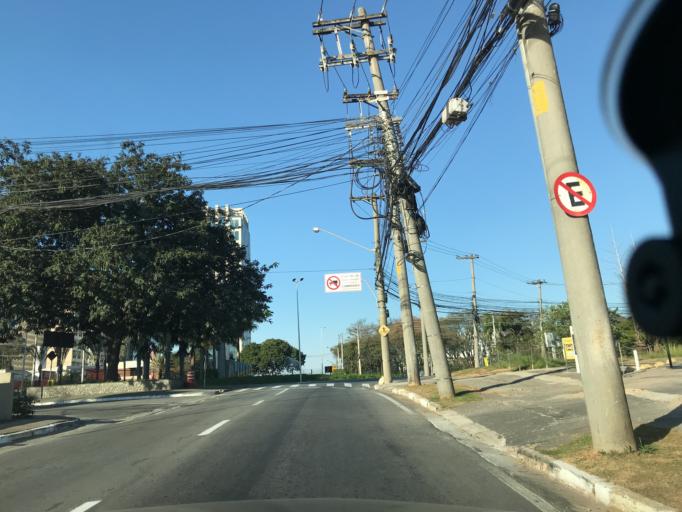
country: BR
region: Sao Paulo
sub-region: Carapicuiba
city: Carapicuiba
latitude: -23.4989
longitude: -46.8492
